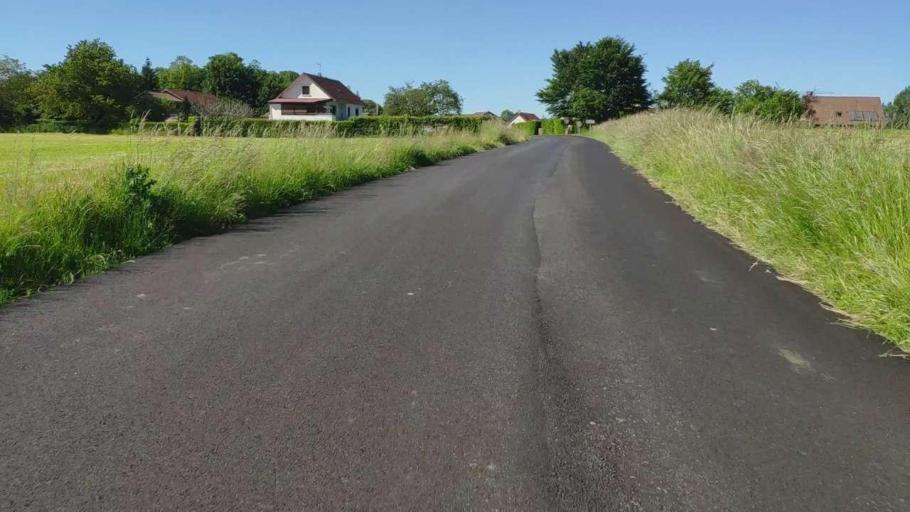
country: FR
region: Franche-Comte
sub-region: Departement du Jura
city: Perrigny
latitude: 46.7165
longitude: 5.5825
